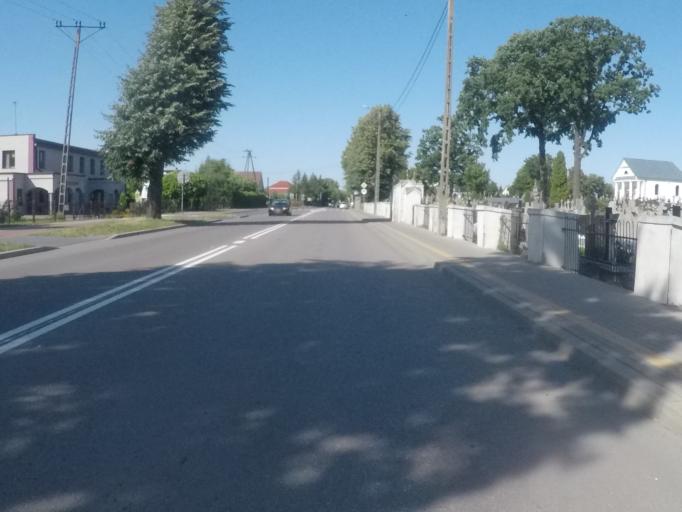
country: PL
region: Podlasie
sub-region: Powiat bielski
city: Bielsk Podlaski
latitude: 52.7581
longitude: 23.1772
